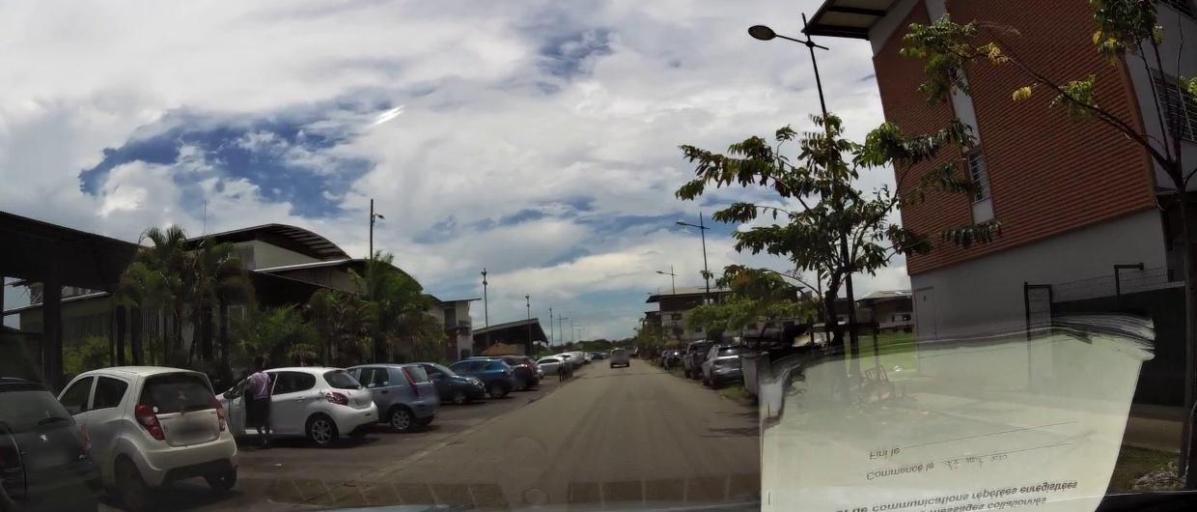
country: GF
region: Guyane
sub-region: Guyane
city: Cayenne
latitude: 4.9331
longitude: -52.3007
